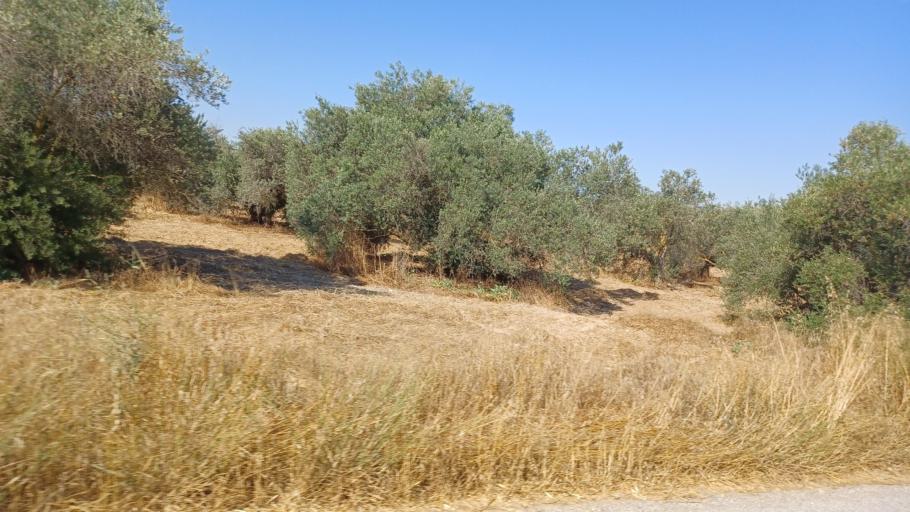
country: CY
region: Larnaka
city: Athienou
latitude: 35.0600
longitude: 33.5199
